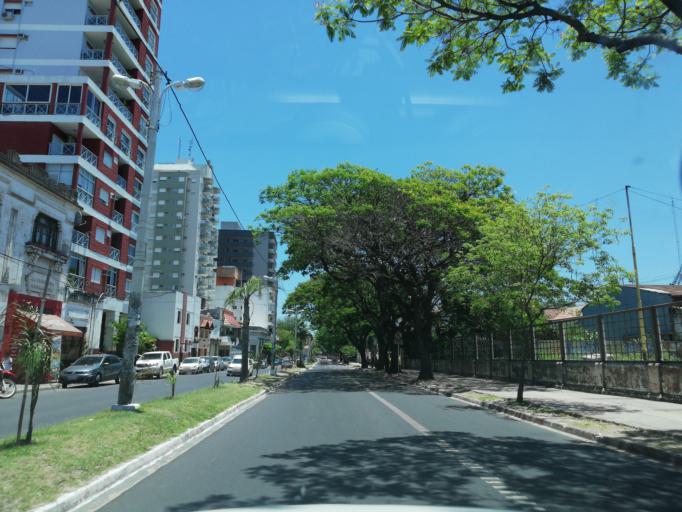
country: AR
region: Corrientes
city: Corrientes
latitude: -27.4610
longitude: -58.8325
